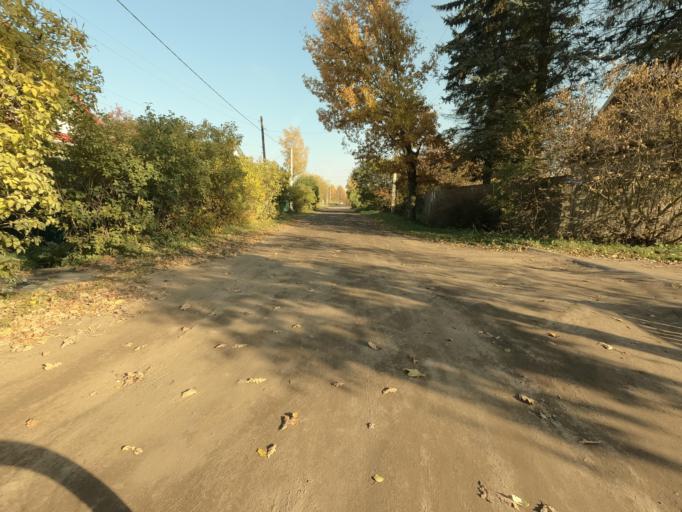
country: RU
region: Leningrad
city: Mga
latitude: 59.7526
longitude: 31.0630
